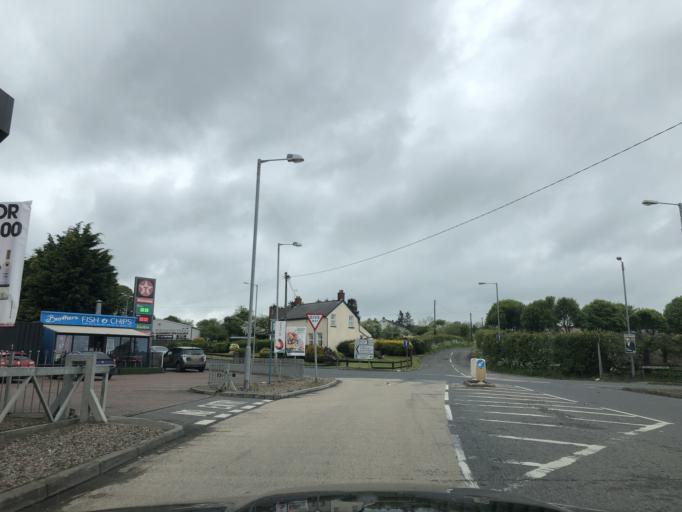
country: GB
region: Northern Ireland
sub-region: Lisburn District
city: Lisburn
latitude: 54.5484
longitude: -6.0762
